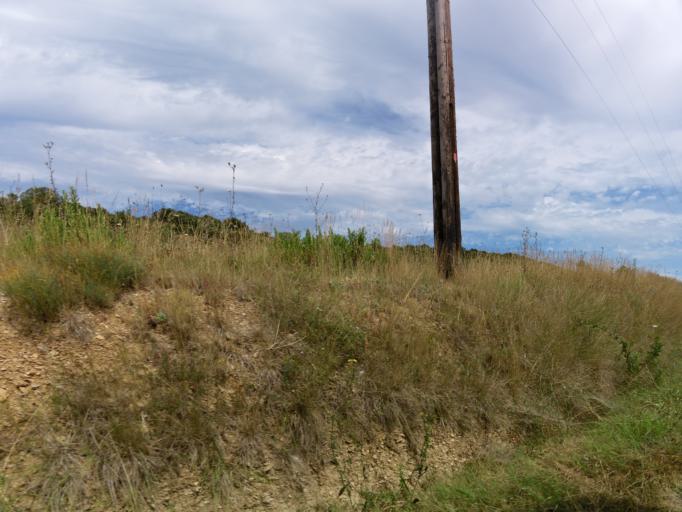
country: FR
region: Languedoc-Roussillon
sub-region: Departement du Gard
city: Congenies
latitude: 43.8064
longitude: 4.1508
